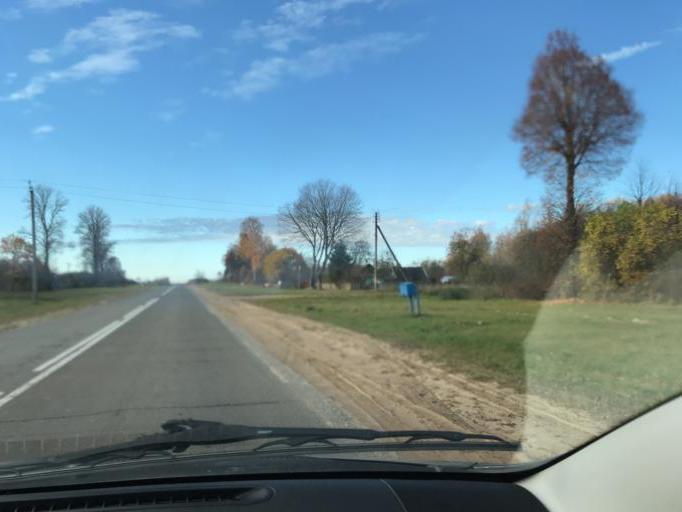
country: BY
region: Vitebsk
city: Haradok
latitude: 55.3629
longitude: 29.5991
